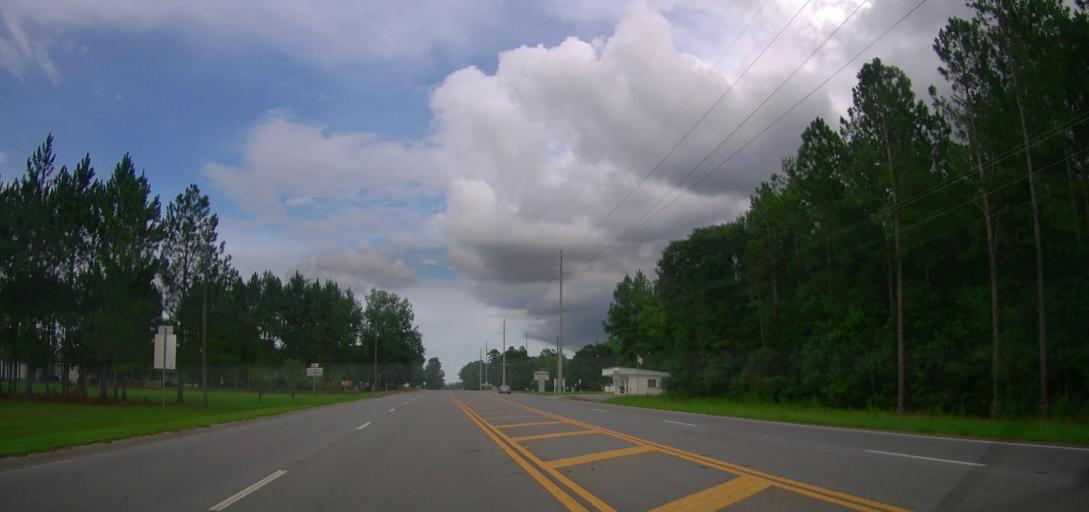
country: US
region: Georgia
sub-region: Pierce County
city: Blackshear
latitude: 31.4067
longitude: -82.1155
